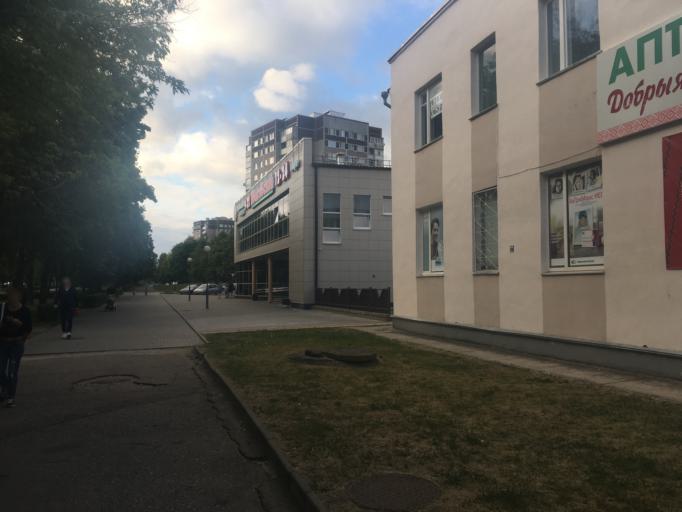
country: BY
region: Grodnenskaya
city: Hrodna
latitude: 53.6903
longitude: 23.8014
